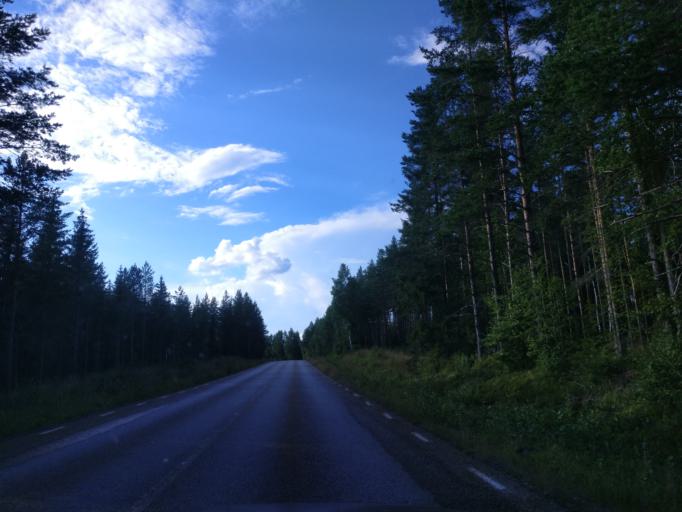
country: SE
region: Dalarna
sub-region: Ludvika Kommun
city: Ludvika
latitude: 60.2899
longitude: 15.1364
